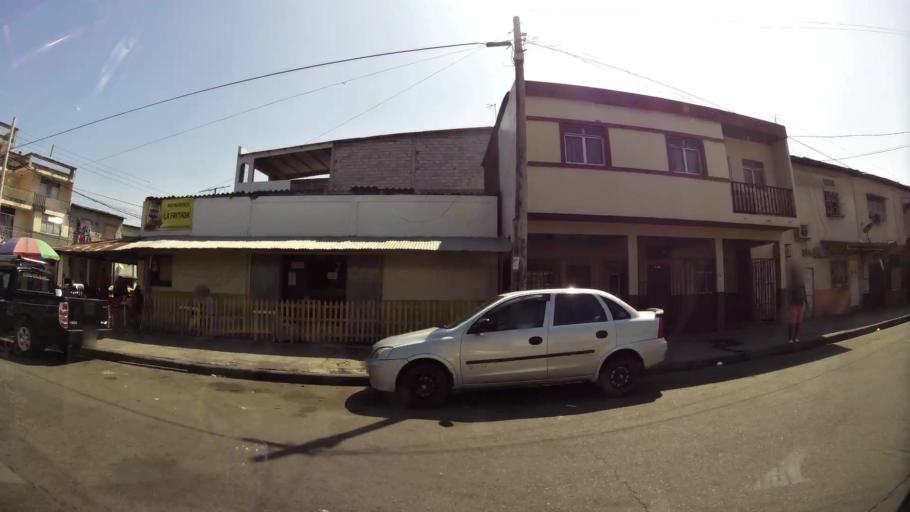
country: EC
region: Guayas
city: Guayaquil
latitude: -2.1928
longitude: -79.9092
